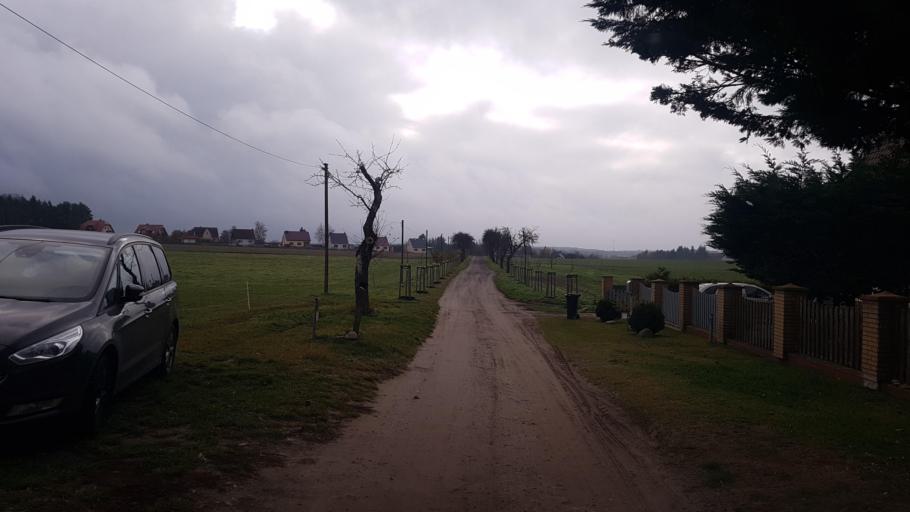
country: DE
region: Brandenburg
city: Roskow
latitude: 52.4273
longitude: 12.7234
